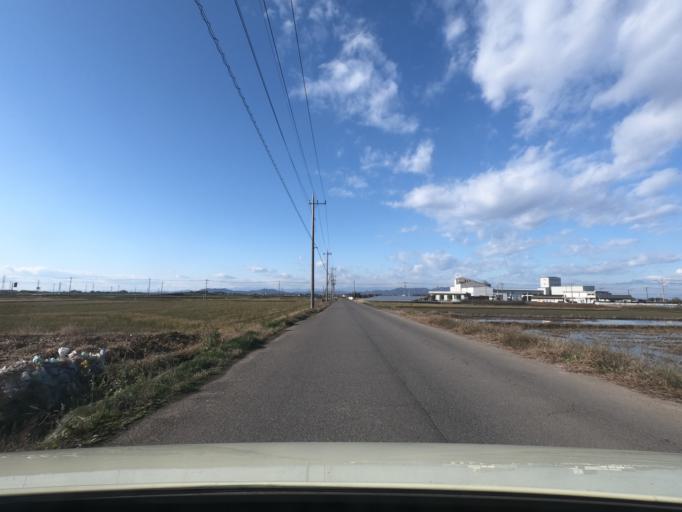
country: JP
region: Ibaraki
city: Koga
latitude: 36.2595
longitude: 139.7295
